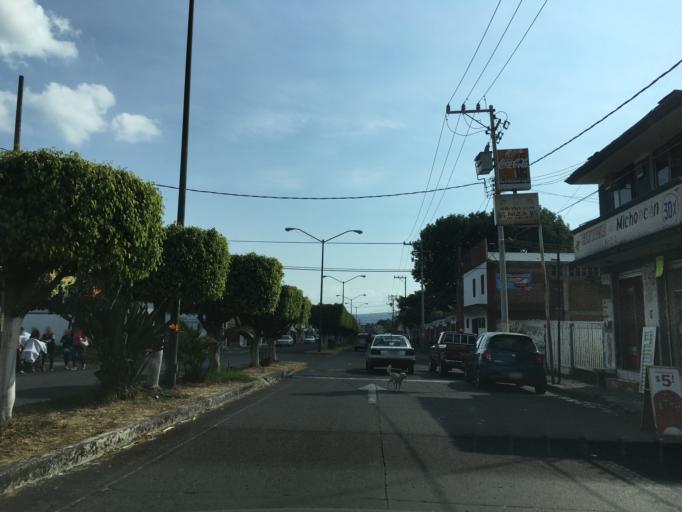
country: MX
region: Michoacan
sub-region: Uruapan
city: Uruapan
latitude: 19.3947
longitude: -102.0531
